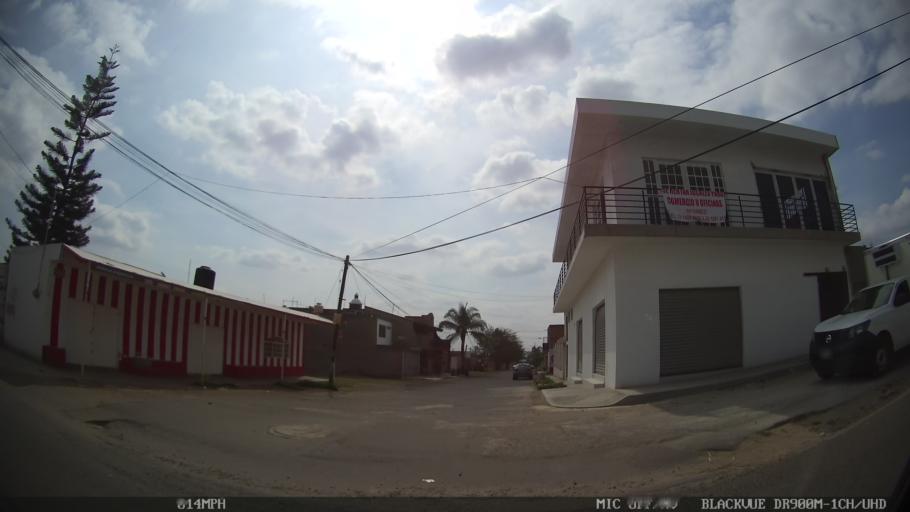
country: MX
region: Jalisco
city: Coyula
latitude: 20.6511
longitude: -103.2215
